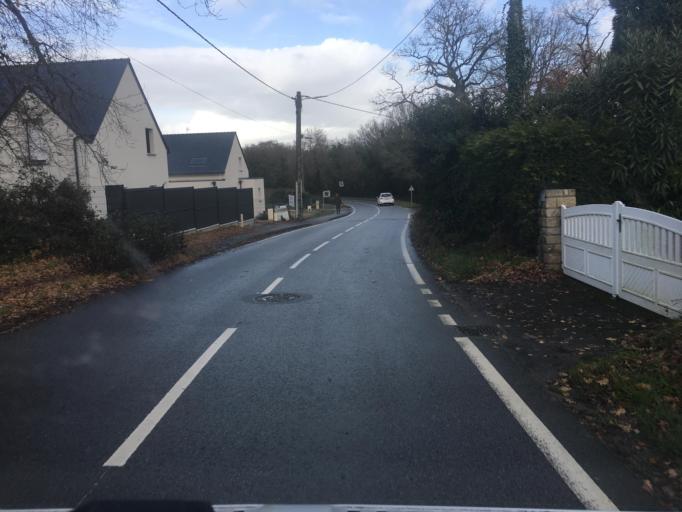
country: FR
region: Brittany
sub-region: Departement du Morbihan
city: Sarzeau
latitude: 47.5151
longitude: -2.7664
